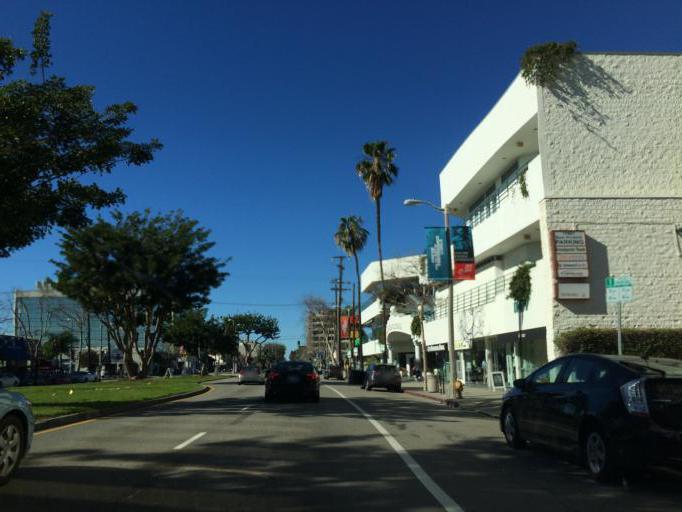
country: US
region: California
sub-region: Los Angeles County
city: Westwood, Los Angeles
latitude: 34.0540
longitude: -118.4644
